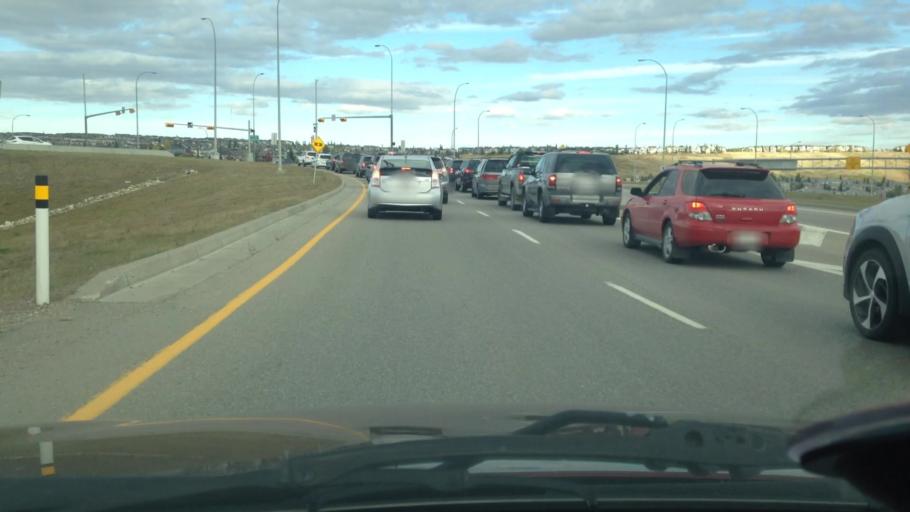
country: CA
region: Alberta
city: Calgary
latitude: 51.1558
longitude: -114.1166
